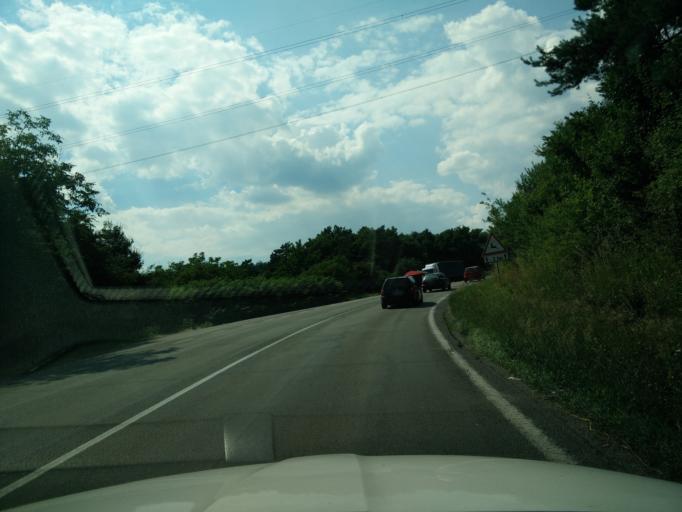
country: SK
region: Nitriansky
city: Novaky
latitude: 48.7195
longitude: 18.5238
